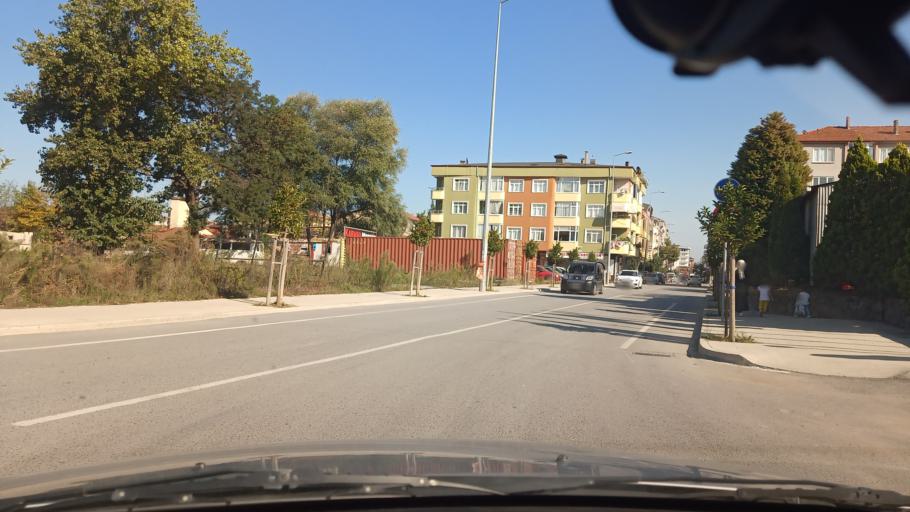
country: TR
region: Sakarya
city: Karasu
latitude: 41.0968
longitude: 30.6877
